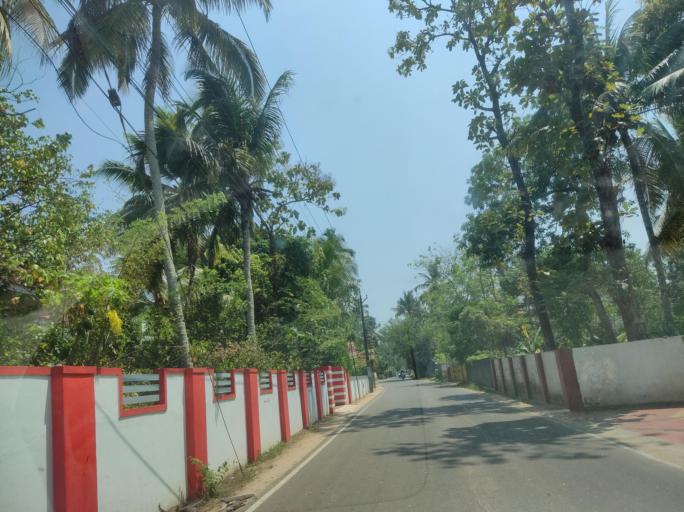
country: IN
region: Kerala
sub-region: Alappuzha
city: Kutiatodu
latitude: 9.8274
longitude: 76.2982
